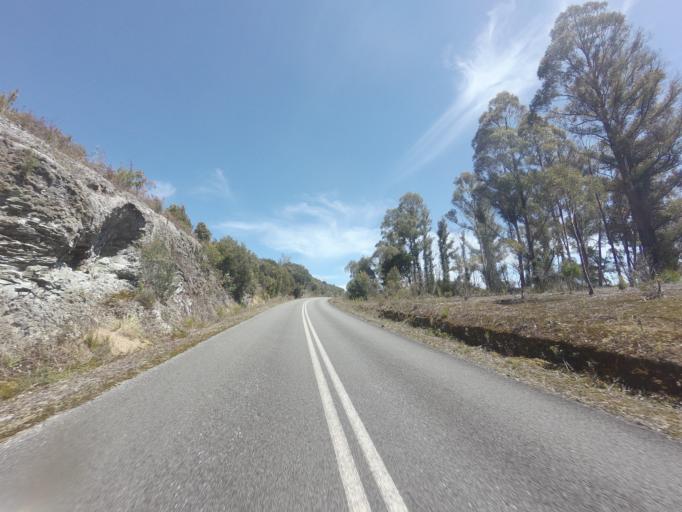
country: AU
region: Tasmania
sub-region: Huon Valley
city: Geeveston
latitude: -42.8463
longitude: 146.2437
